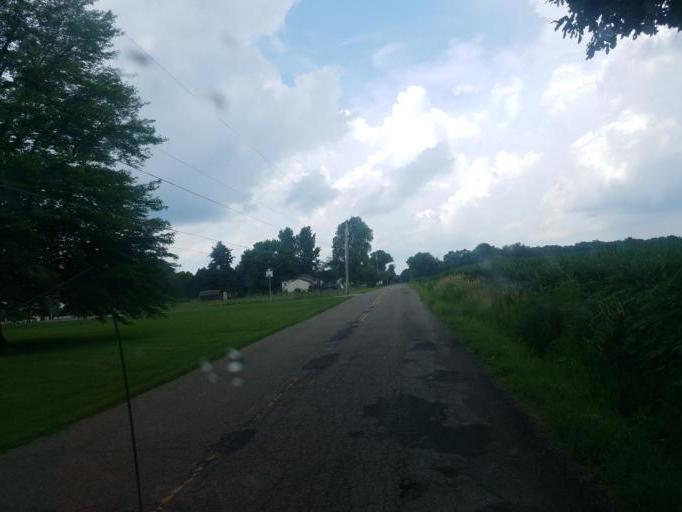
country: US
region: Ohio
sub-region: Columbiana County
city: Leetonia
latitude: 40.9368
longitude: -80.7452
